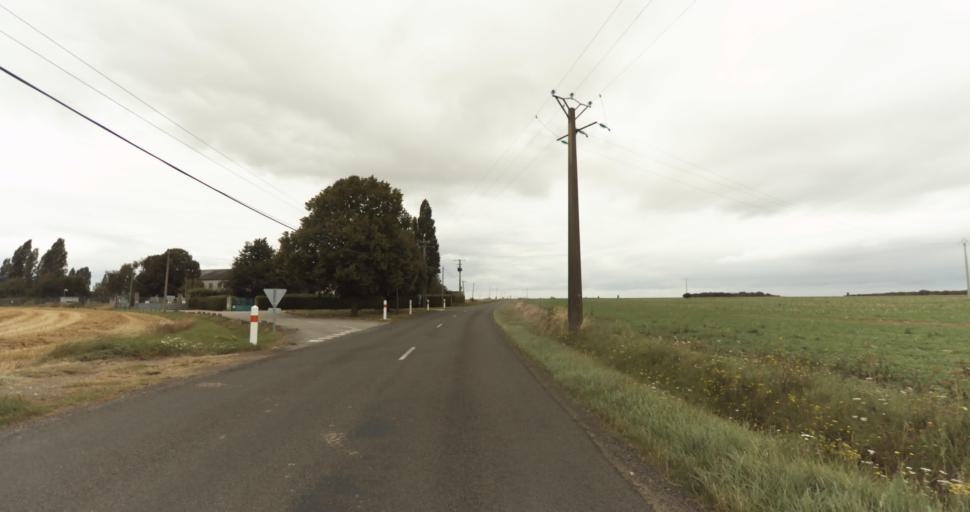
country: FR
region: Haute-Normandie
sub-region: Departement de l'Eure
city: Gravigny
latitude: 49.0430
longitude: 1.2117
